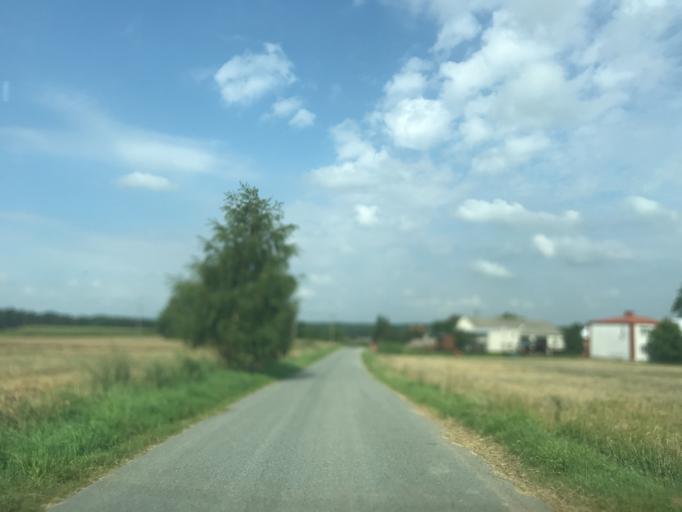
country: PL
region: Warmian-Masurian Voivodeship
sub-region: Powiat nowomiejski
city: Kurzetnik
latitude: 53.4004
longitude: 19.4612
